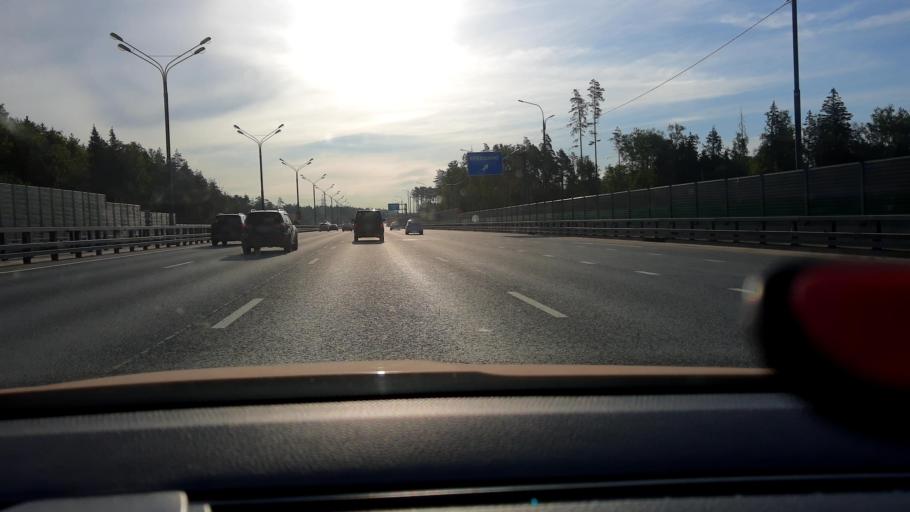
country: RU
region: Moskovskaya
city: Zhavoronki
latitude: 55.6139
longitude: 37.0881
